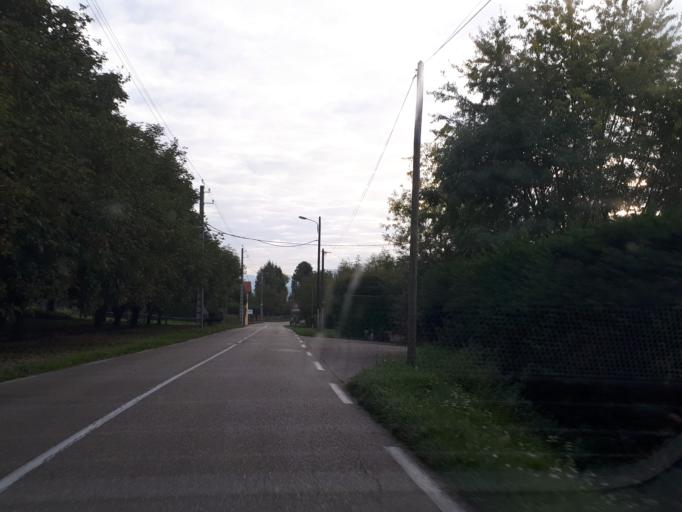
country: FR
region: Rhone-Alpes
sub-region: Departement de l'Isere
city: Saint-Cassien
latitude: 45.3539
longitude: 5.5422
